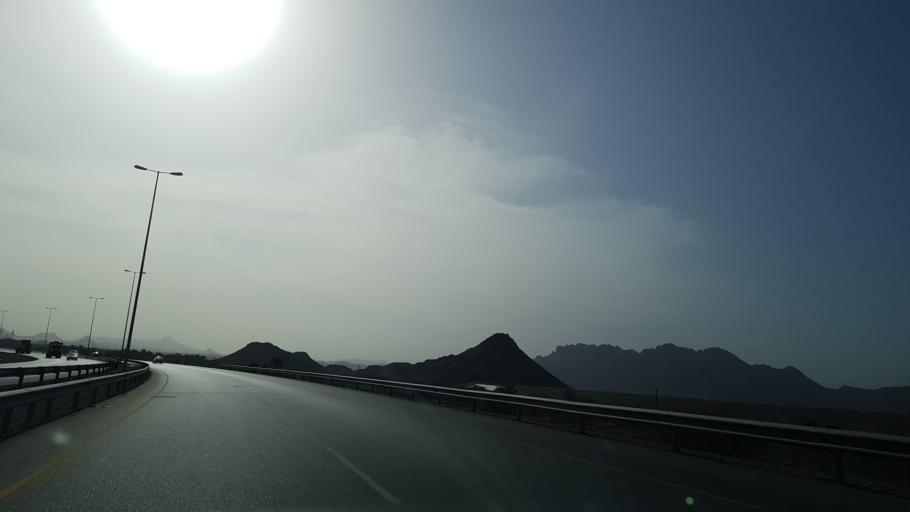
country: OM
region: Muhafazat ad Dakhiliyah
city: Nizwa
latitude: 22.8627
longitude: 57.5829
